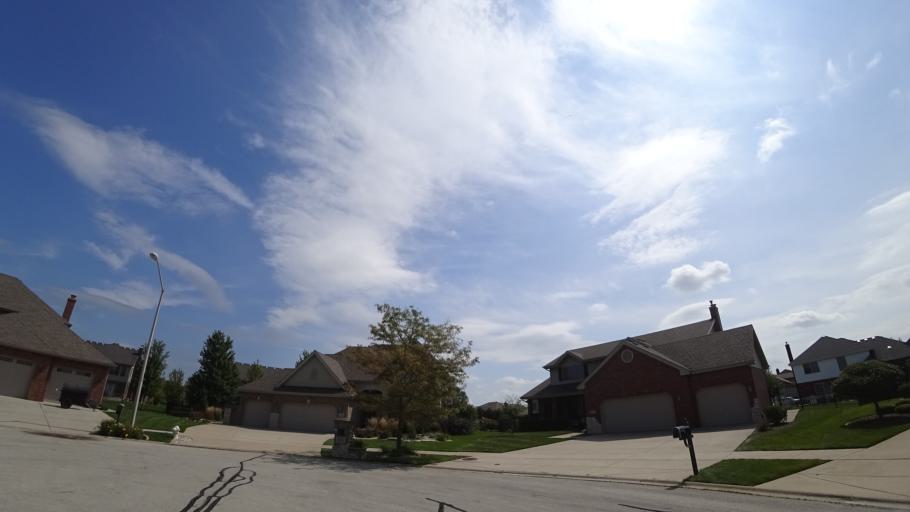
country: US
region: Illinois
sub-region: Cook County
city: Orland Hills
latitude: 41.5689
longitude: -87.8258
